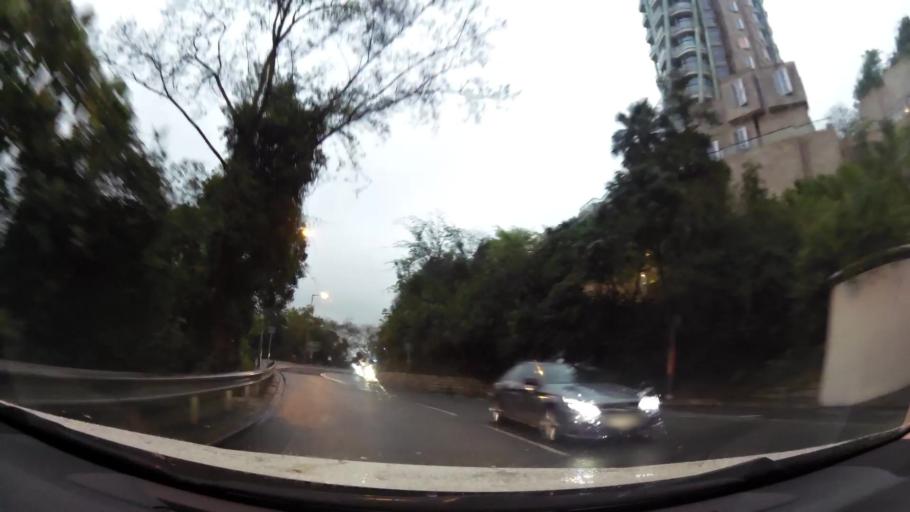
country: HK
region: Wanchai
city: Wan Chai
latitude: 22.2689
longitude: 114.1738
